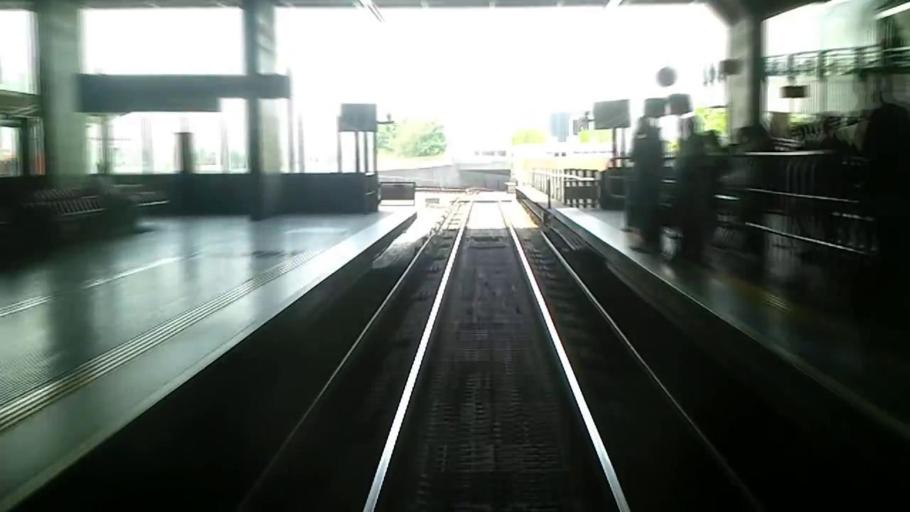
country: BR
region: Sao Paulo
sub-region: Sao Paulo
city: Sao Paulo
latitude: -23.5262
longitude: -46.6669
